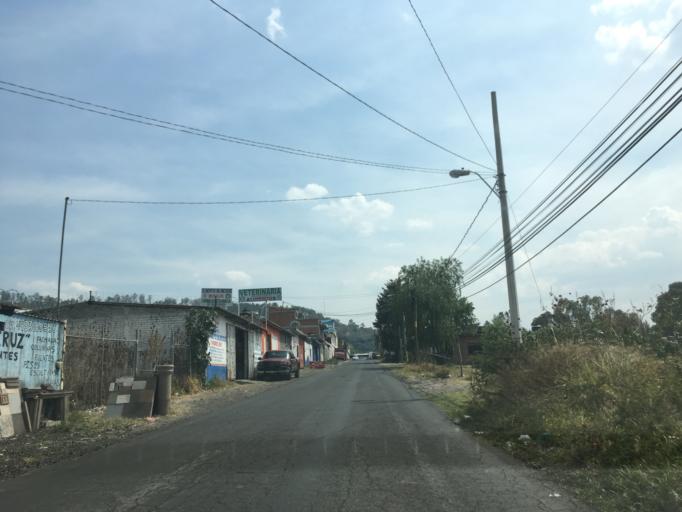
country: MX
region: Michoacan
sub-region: Morelia
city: Morelos
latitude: 19.6477
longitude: -101.2489
